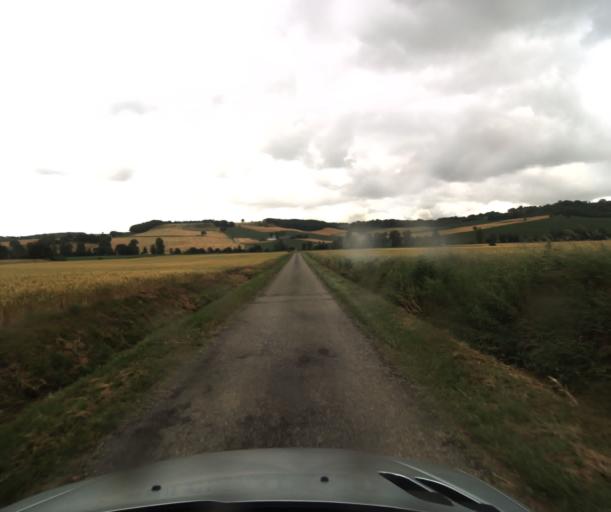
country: FR
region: Midi-Pyrenees
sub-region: Departement du Tarn-et-Garonne
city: Lavit
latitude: 43.9506
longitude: 0.9338
